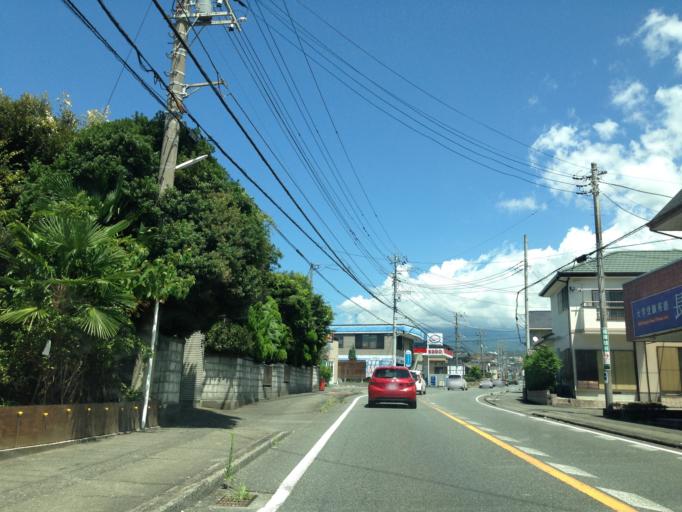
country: JP
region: Shizuoka
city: Fuji
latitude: 35.1709
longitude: 138.6897
